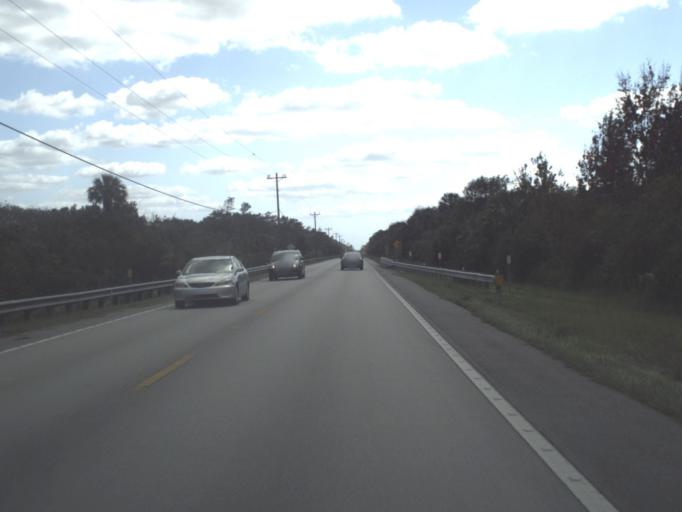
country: US
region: Florida
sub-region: Collier County
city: Marco
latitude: 25.8993
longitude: -81.2892
